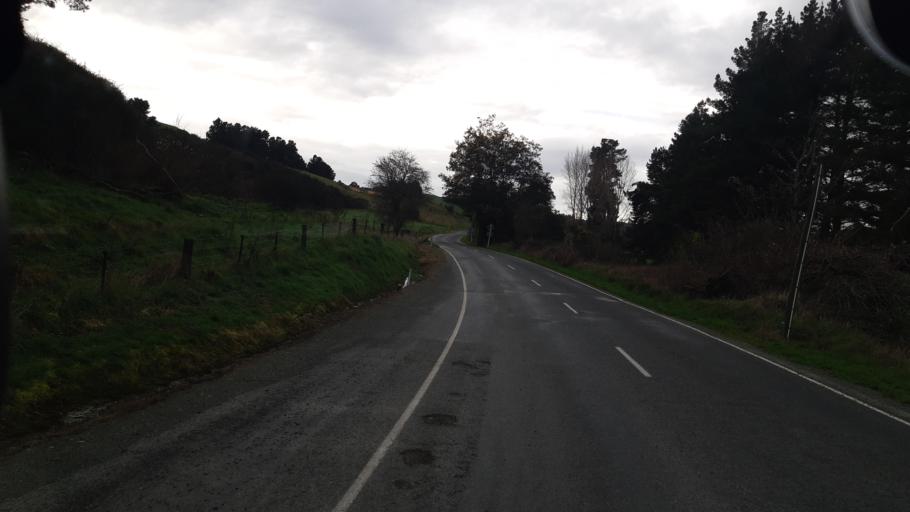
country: NZ
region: Tasman
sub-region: Tasman District
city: Motueka
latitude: -41.2791
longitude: 172.8588
